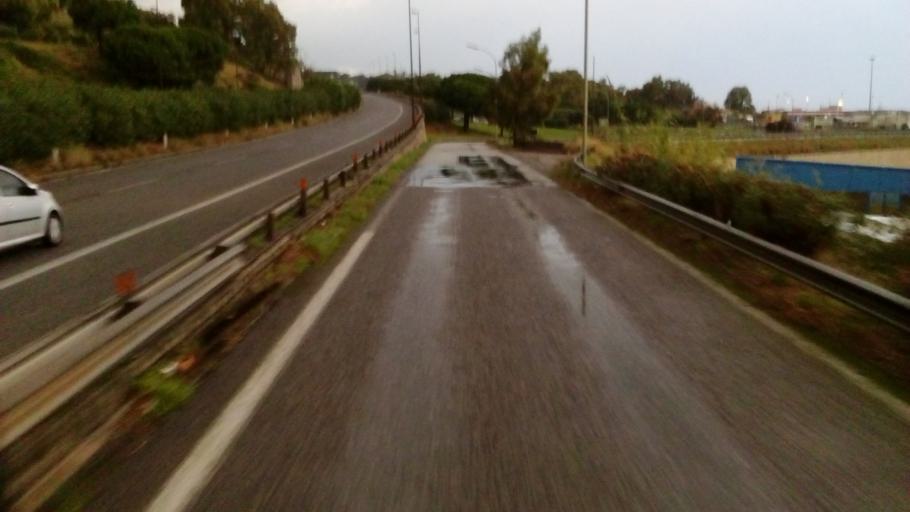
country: IT
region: Sicily
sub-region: Messina
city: Larderia
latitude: 38.1312
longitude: 15.5196
